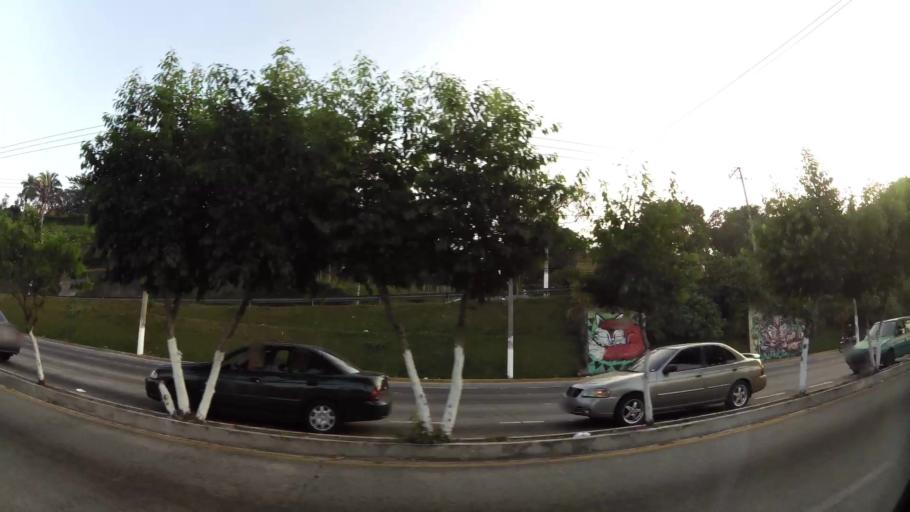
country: SV
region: San Salvador
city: San Salvador
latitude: 13.6791
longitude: -89.2116
